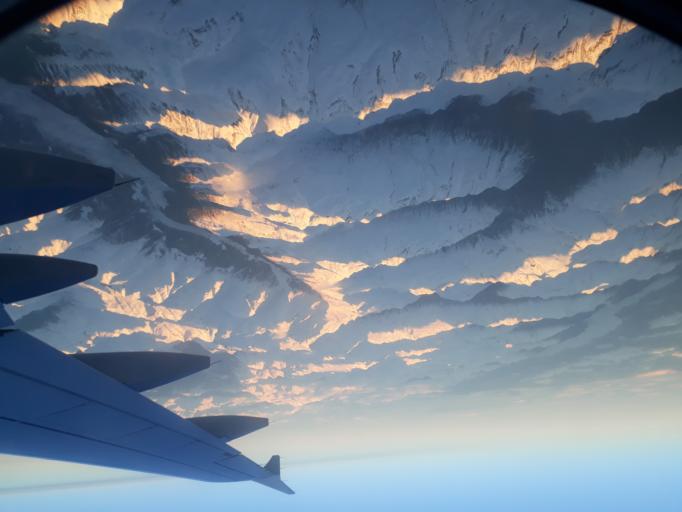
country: AT
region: Tyrol
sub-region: Politischer Bezirk Schwaz
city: Mayrhofen
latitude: 47.0522
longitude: 11.8645
